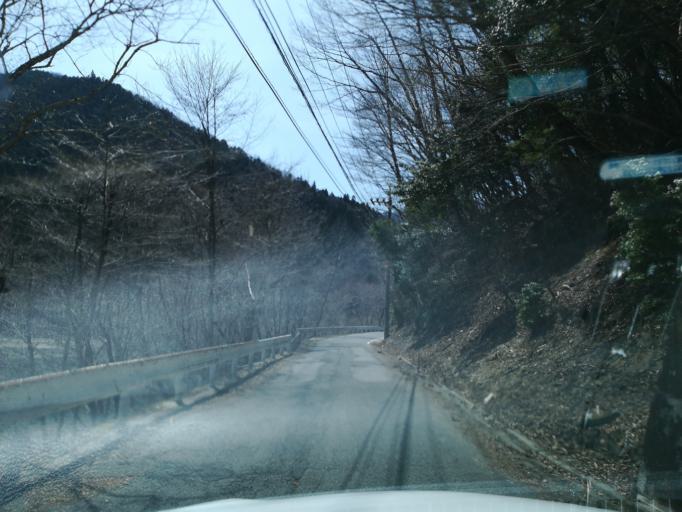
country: JP
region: Tokushima
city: Wakimachi
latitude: 33.8515
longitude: 134.0309
